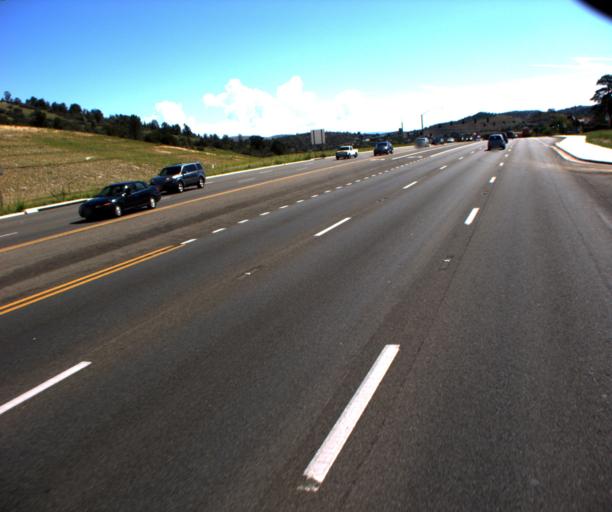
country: US
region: Arizona
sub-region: Yavapai County
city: Prescott
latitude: 34.5491
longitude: -112.4405
